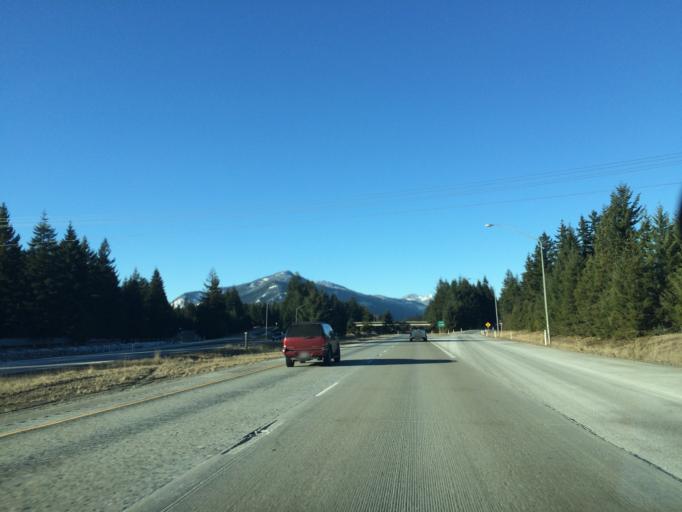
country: US
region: Washington
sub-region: Kittitas County
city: Cle Elum
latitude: 47.2468
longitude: -121.1856
